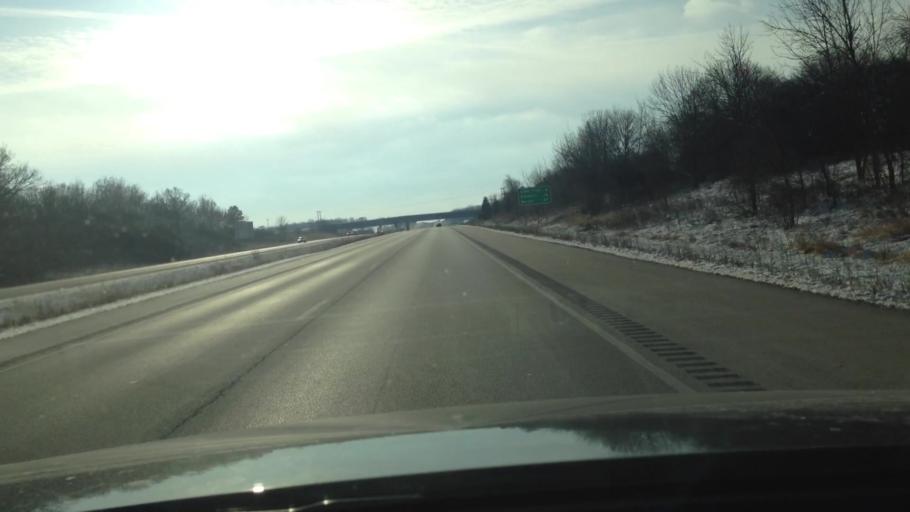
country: US
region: Wisconsin
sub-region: Waukesha County
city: Mukwonago
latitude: 42.8446
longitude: -88.3315
